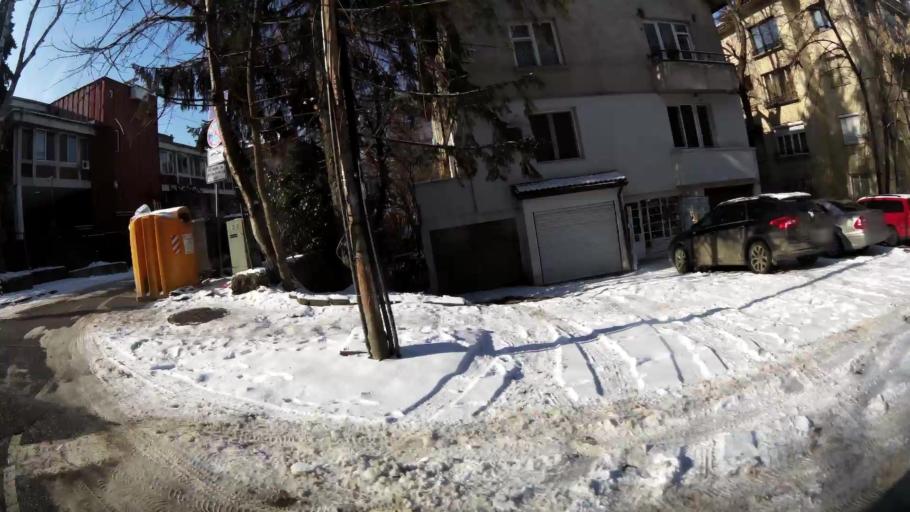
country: BG
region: Sofia-Capital
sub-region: Stolichna Obshtina
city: Sofia
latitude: 42.6759
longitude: 23.3251
